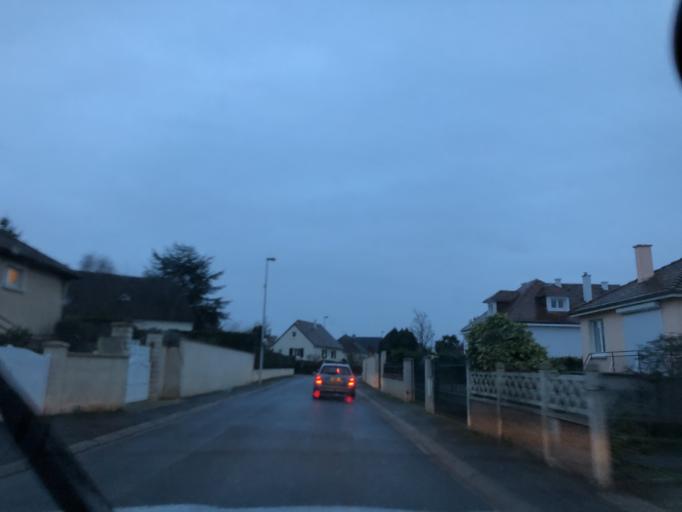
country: FR
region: Lower Normandy
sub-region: Departement du Calvados
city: Beuville
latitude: 49.2437
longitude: -0.3301
